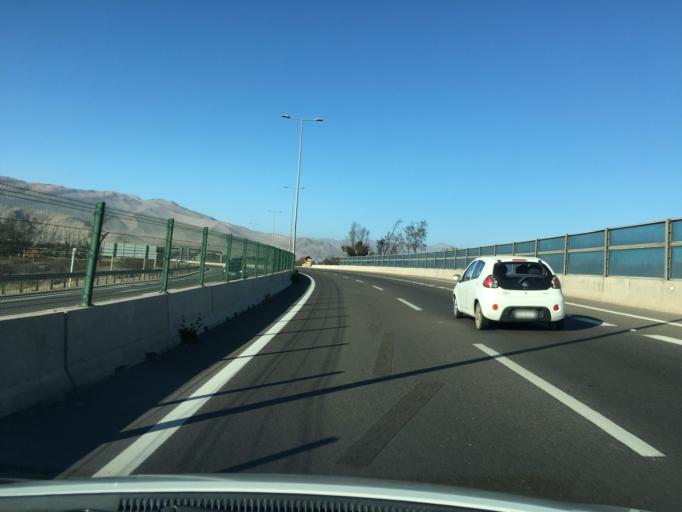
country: CL
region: Atacama
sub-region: Provincia de Copiapo
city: Copiapo
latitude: -27.3106
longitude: -70.4956
